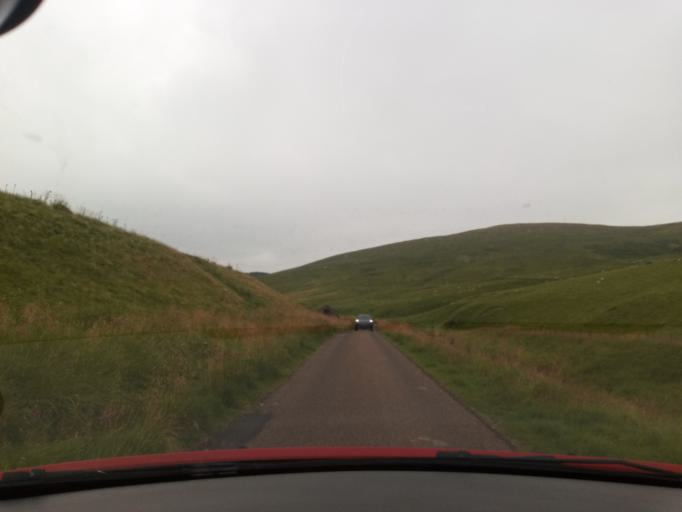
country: GB
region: England
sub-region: Northumberland
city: Rochester
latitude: 55.3937
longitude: -2.2415
